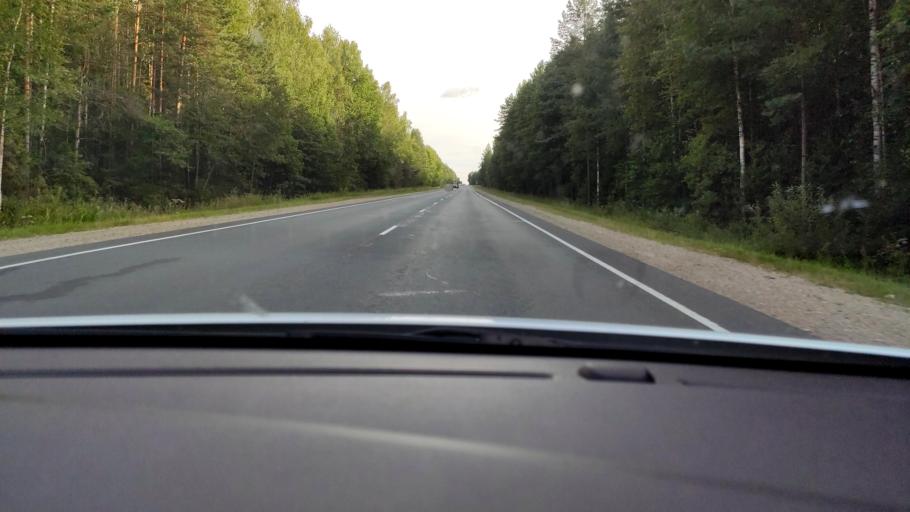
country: RU
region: Mariy-El
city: Suslonger
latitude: 56.2663
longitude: 48.2328
